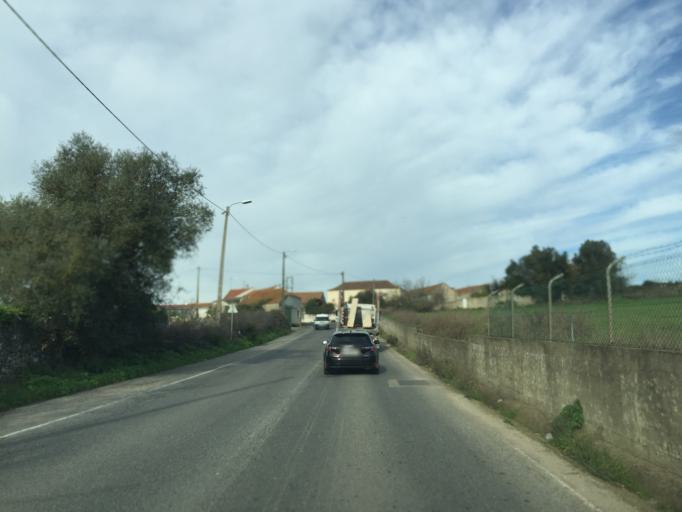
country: PT
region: Lisbon
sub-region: Sintra
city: Pero Pinheiro
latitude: 38.8612
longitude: -9.3088
